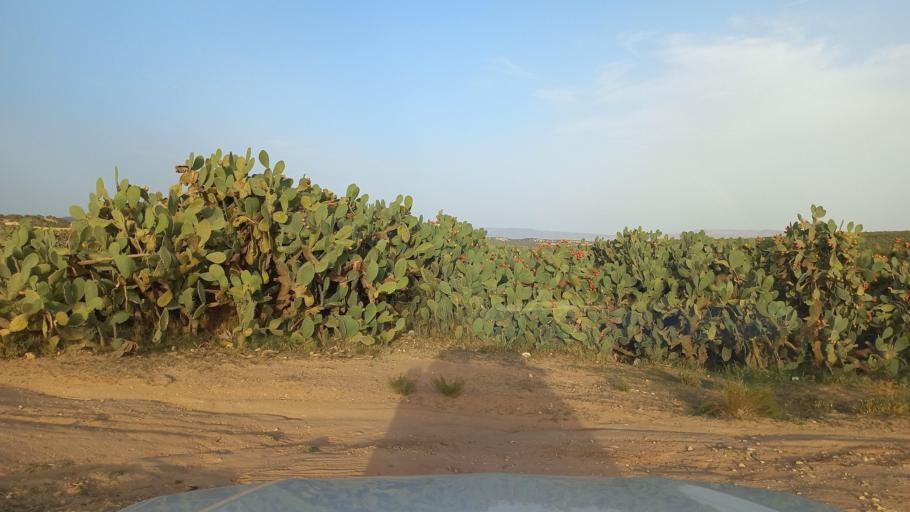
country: TN
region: Al Qasrayn
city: Sbiba
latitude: 35.4098
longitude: 8.9014
